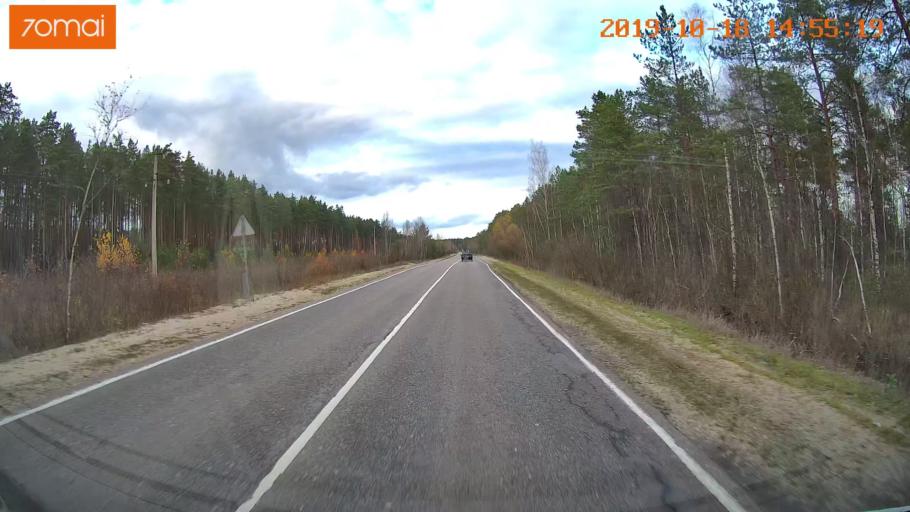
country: RU
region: Vladimir
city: Kurlovo
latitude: 55.4503
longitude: 40.5885
